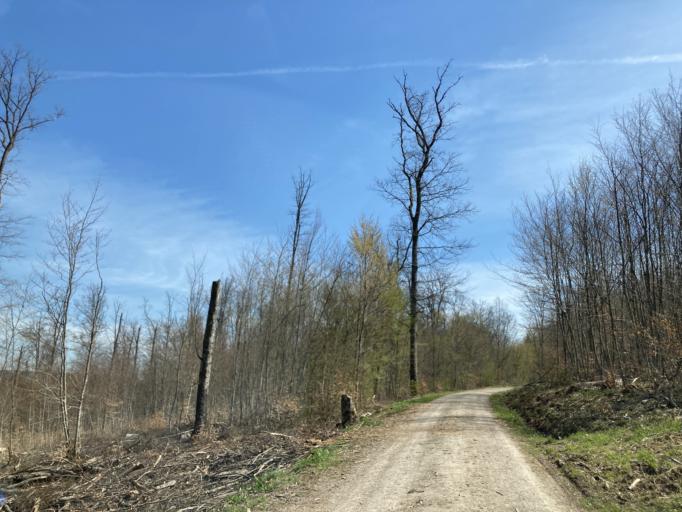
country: DE
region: Baden-Wuerttemberg
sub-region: Tuebingen Region
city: Tuebingen
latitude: 48.5560
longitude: 9.0520
